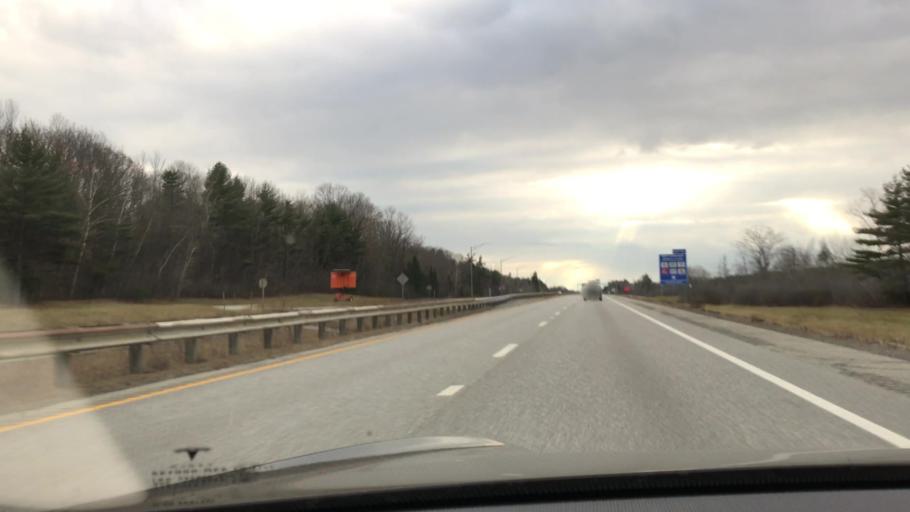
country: US
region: Maine
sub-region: Kennebec County
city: Gardiner
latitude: 44.2293
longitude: -69.8133
